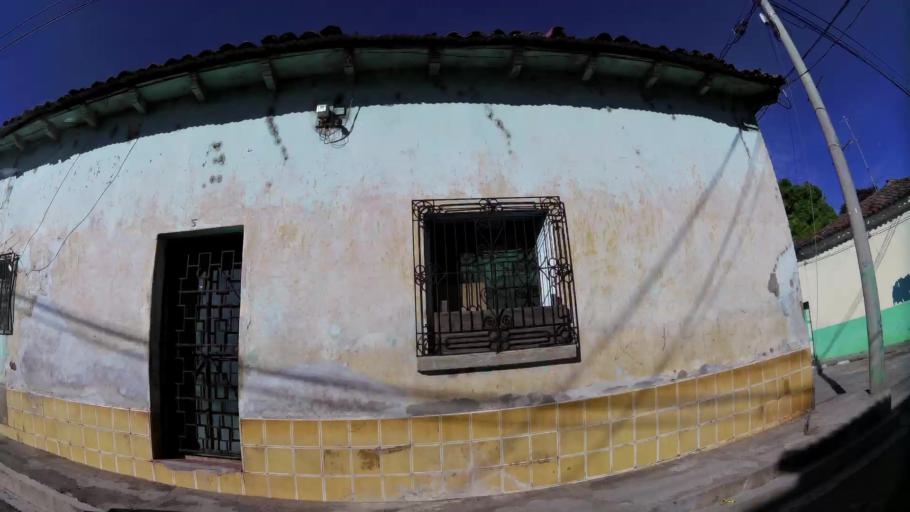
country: SV
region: Santa Ana
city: Santa Ana
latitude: 13.9987
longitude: -89.5556
